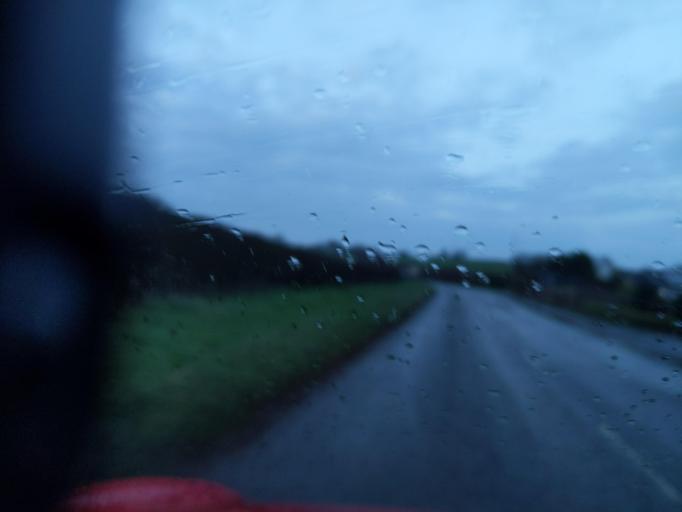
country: GB
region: England
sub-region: Devon
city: Wembury
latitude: 50.3407
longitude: -4.0741
